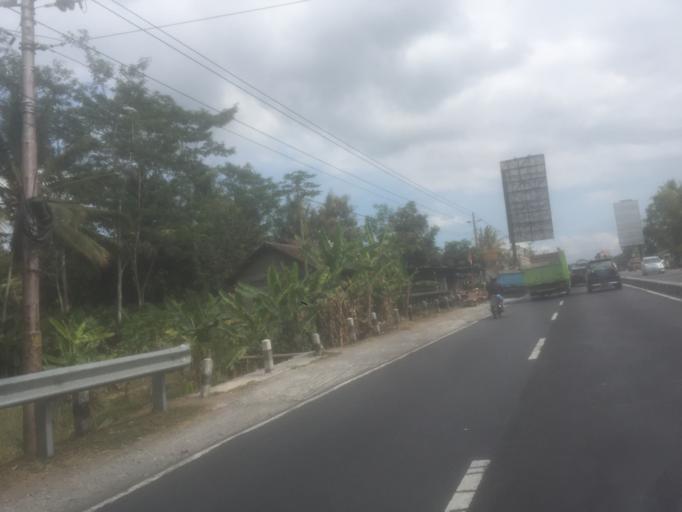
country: ID
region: Central Java
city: Muntilan
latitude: -7.6234
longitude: 110.3133
